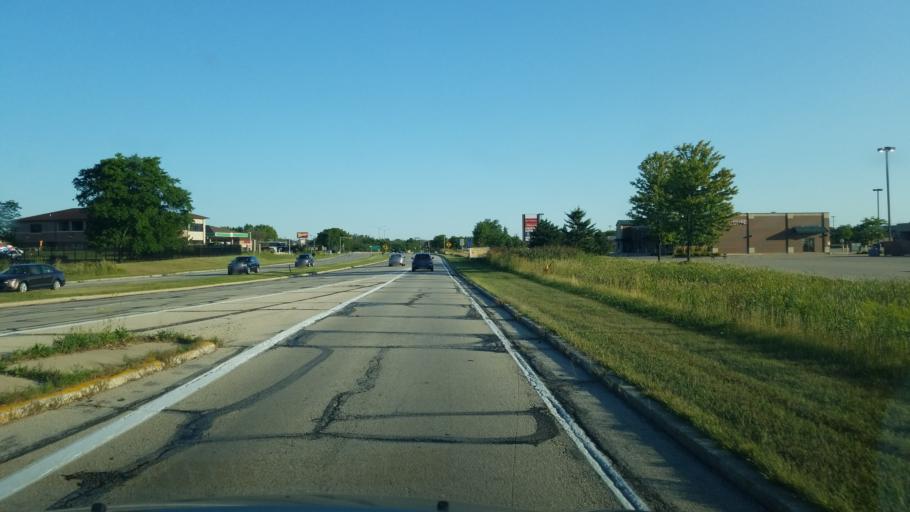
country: US
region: Wisconsin
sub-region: Milwaukee County
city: Brown Deer
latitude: 43.1805
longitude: -87.9621
